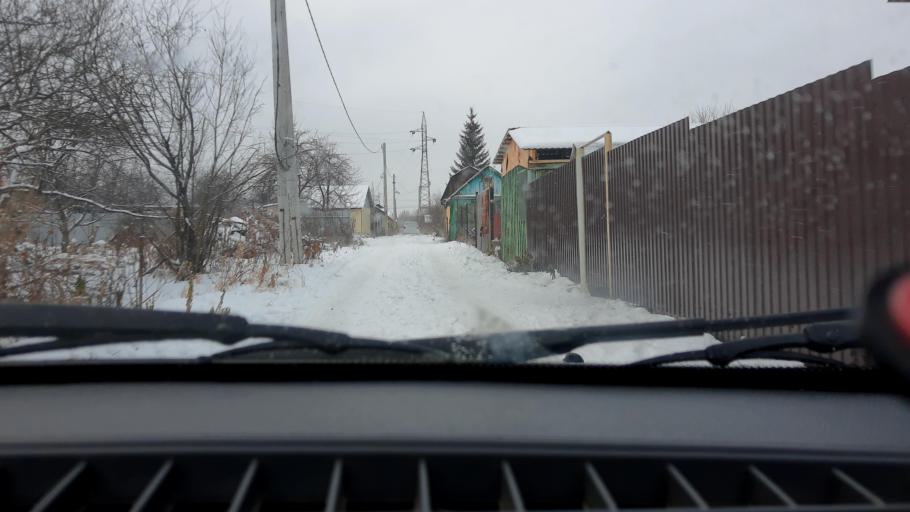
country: RU
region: Bashkortostan
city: Ufa
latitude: 54.8256
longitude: 56.1276
